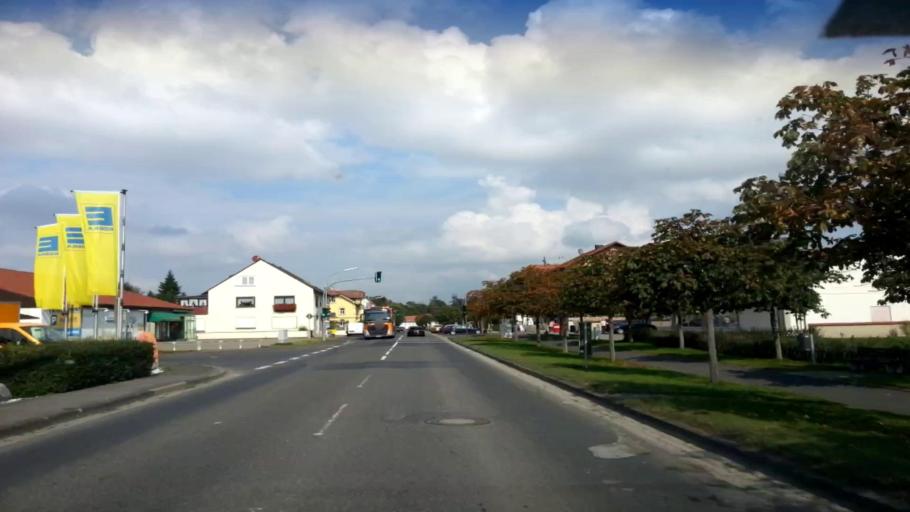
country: DE
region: Bavaria
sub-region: Regierungsbezirk Unterfranken
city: Wiesentheid
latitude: 49.7895
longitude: 10.3408
